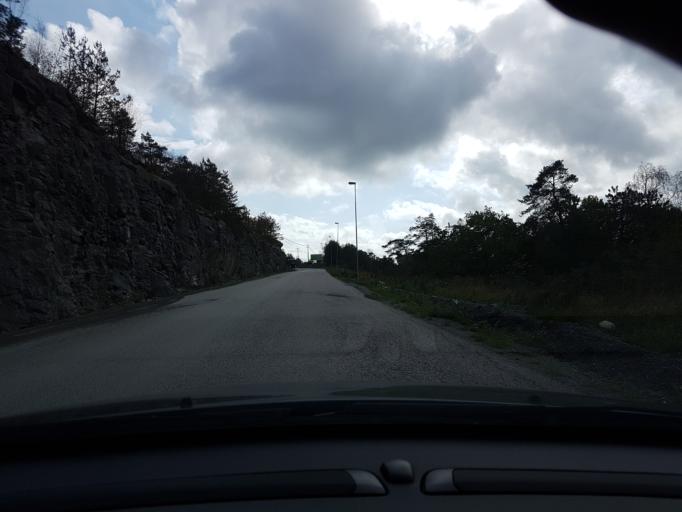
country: SE
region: Vaestra Goetaland
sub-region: Ale Kommun
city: Surte
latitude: 57.8689
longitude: 12.0346
